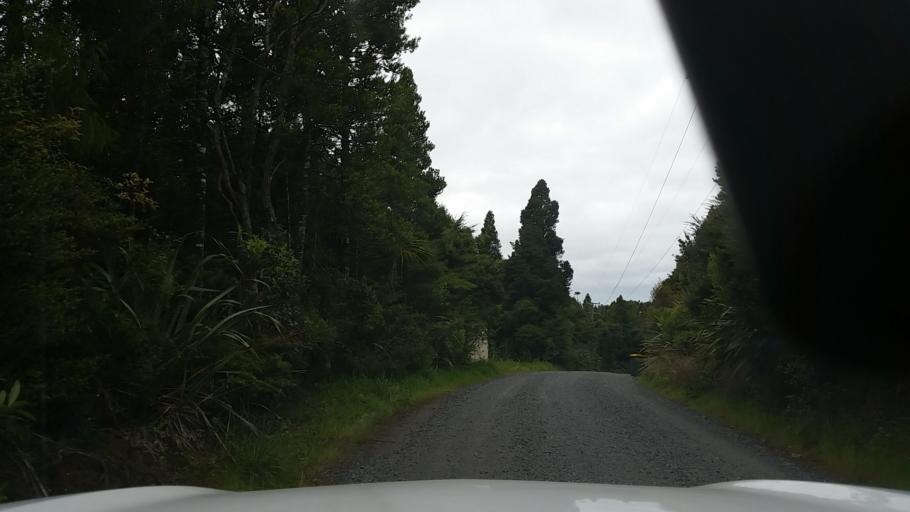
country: NZ
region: Auckland
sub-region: Auckland
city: Muriwai Beach
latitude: -36.8747
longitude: 174.4831
